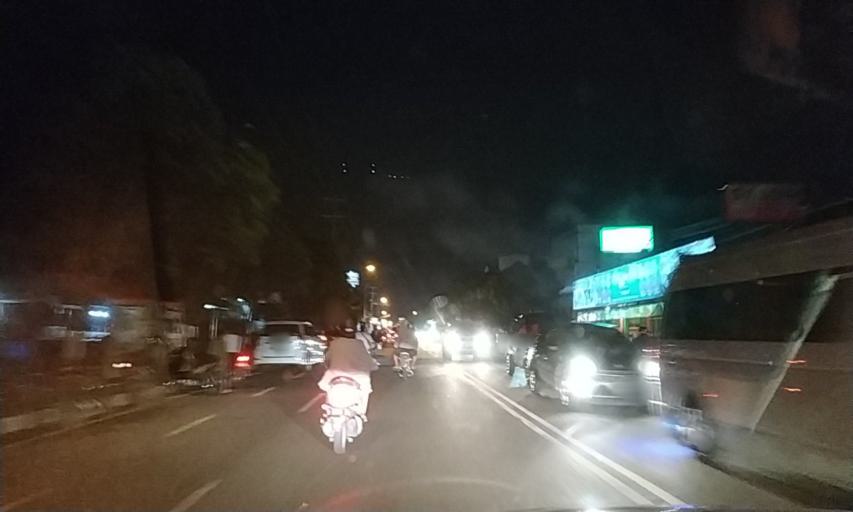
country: ID
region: Daerah Istimewa Yogyakarta
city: Yogyakarta
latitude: -7.7948
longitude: 110.3531
